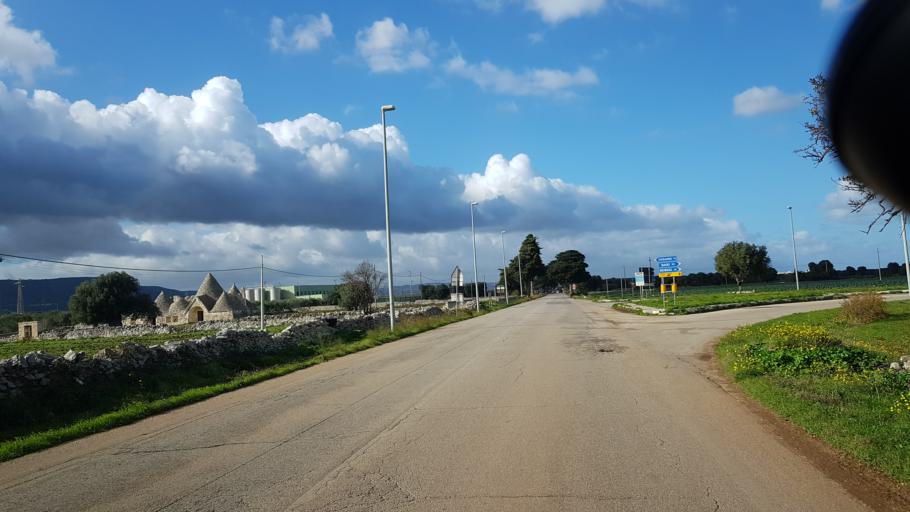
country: IT
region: Apulia
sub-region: Provincia di Brindisi
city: Montalbano
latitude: 40.7863
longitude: 17.4717
